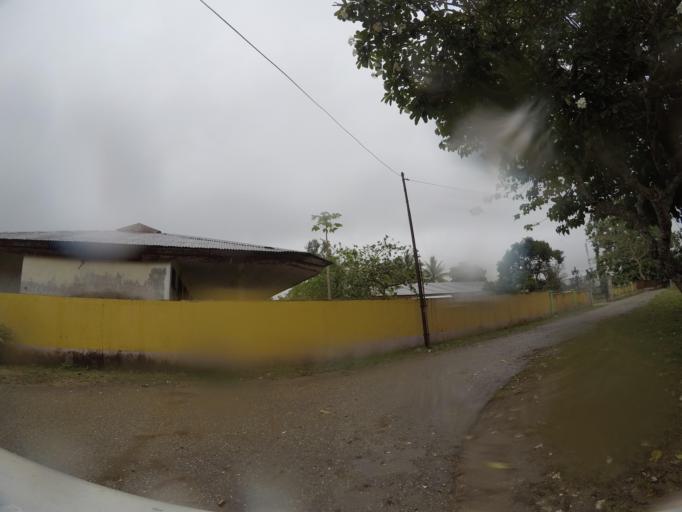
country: TL
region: Lautem
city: Lospalos
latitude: -8.5217
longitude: 126.9968
